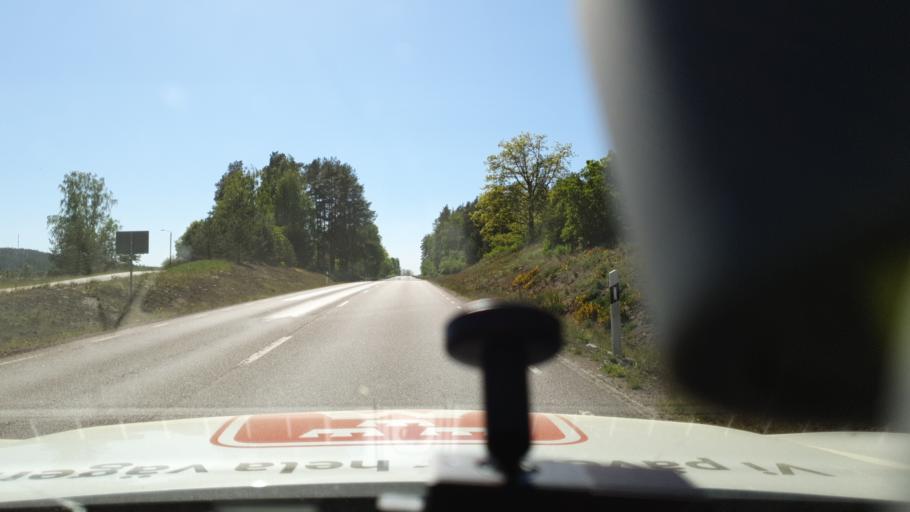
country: SE
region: Kalmar
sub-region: Hultsfreds Kommun
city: Virserum
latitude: 57.4100
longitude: 15.5899
